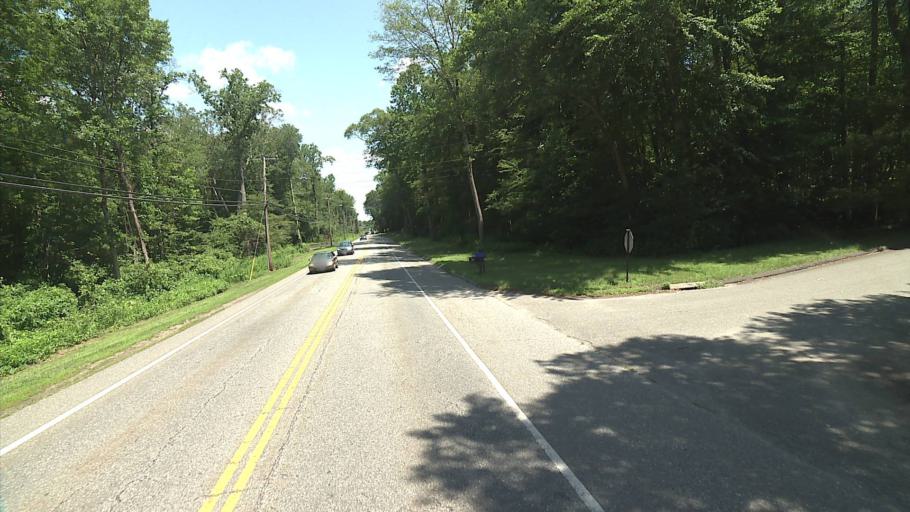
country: US
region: Connecticut
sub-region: Middlesex County
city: Old Saybrook
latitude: 41.3167
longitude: -72.3815
